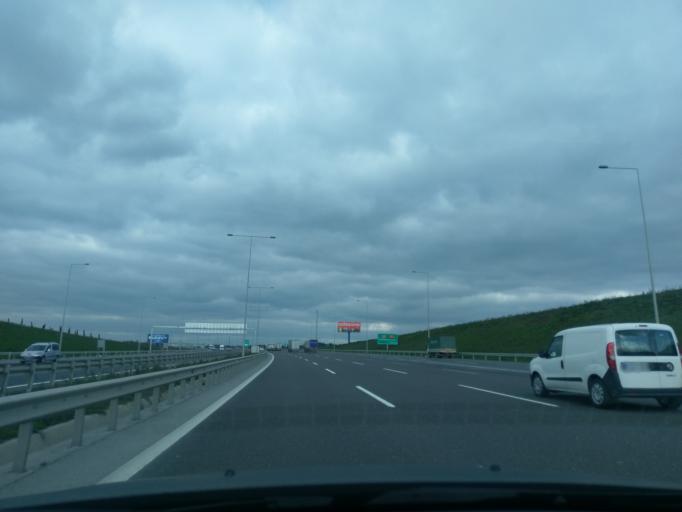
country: TR
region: Istanbul
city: Basaksehir
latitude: 41.1208
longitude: 28.8137
